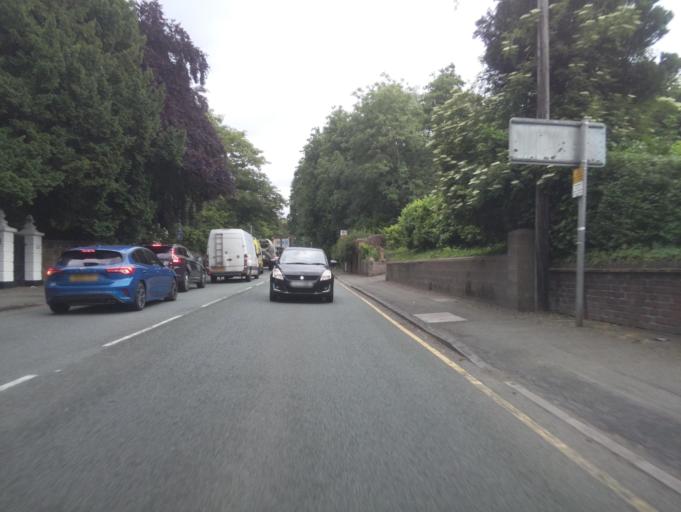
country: GB
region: England
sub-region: Wolverhampton
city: Wolverhampton
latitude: 52.5679
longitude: -2.1445
